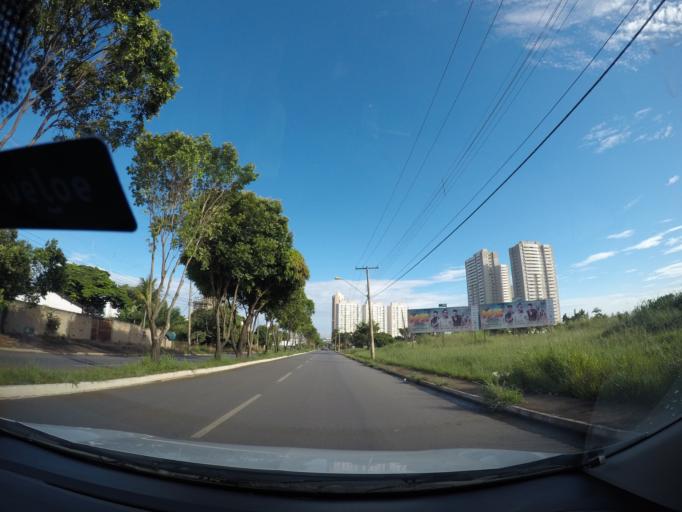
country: BR
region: Goias
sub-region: Goiania
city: Goiania
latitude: -16.7399
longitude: -49.2847
